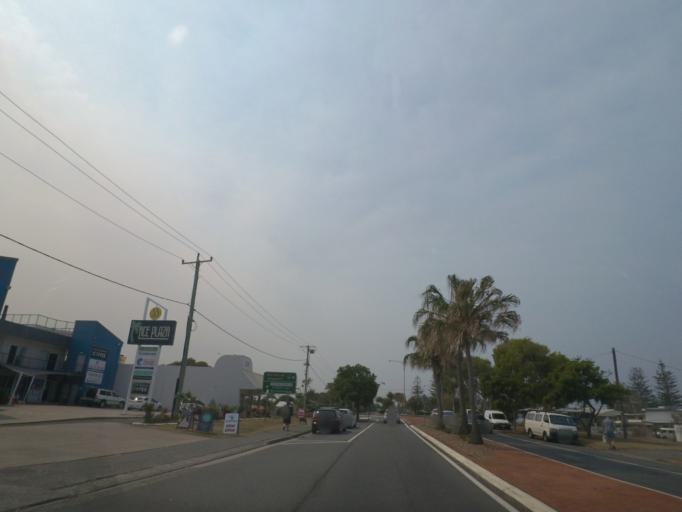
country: AU
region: New South Wales
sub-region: Tweed
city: Casuarina
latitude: -28.3314
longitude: 153.5693
